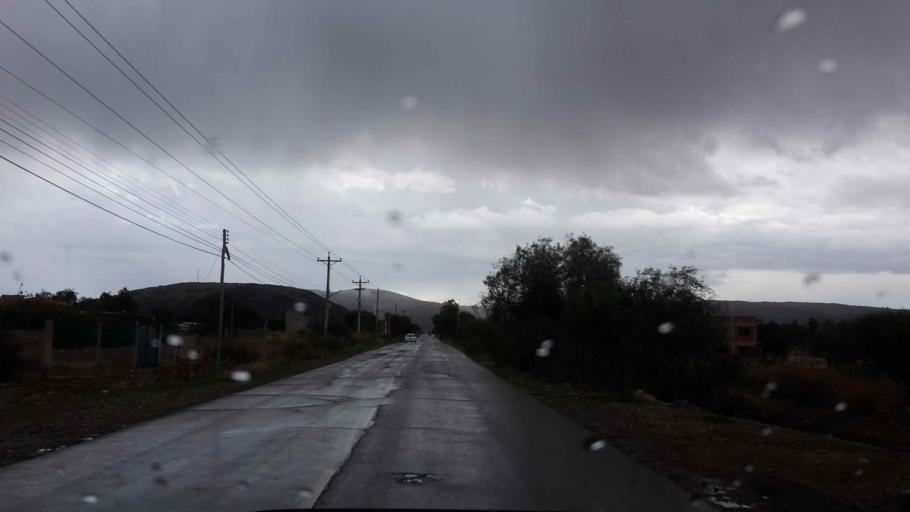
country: BO
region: Cochabamba
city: Tarata
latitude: -17.5598
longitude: -66.0832
